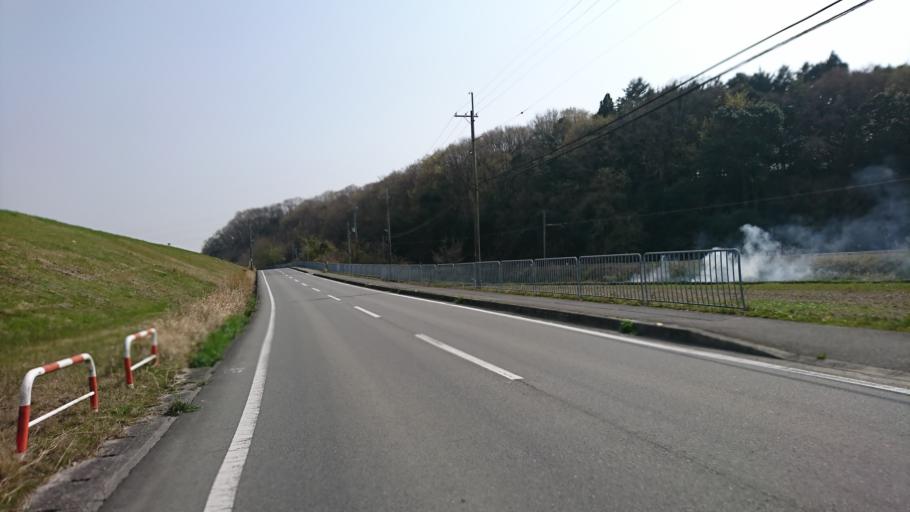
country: JP
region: Hyogo
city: Ono
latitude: 34.8474
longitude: 134.9101
